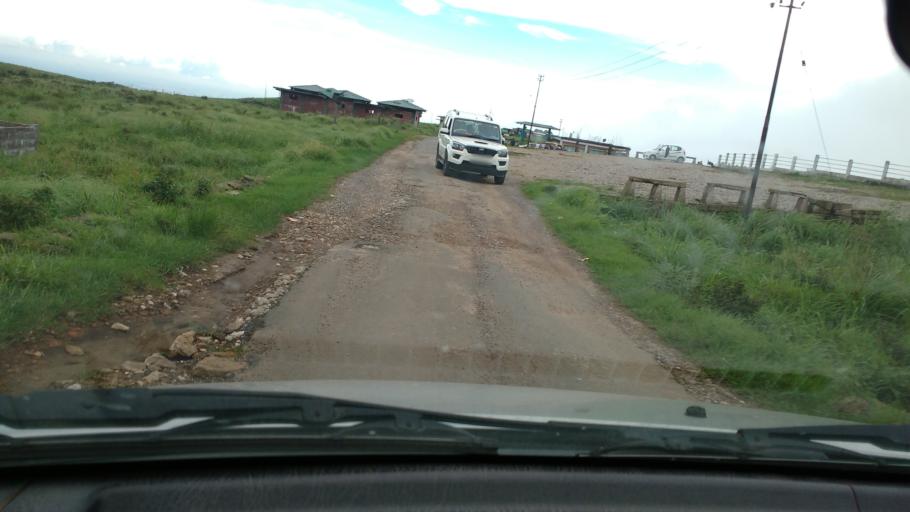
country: IN
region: Meghalaya
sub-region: East Khasi Hills
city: Cherrapunji
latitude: 25.2727
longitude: 91.6909
